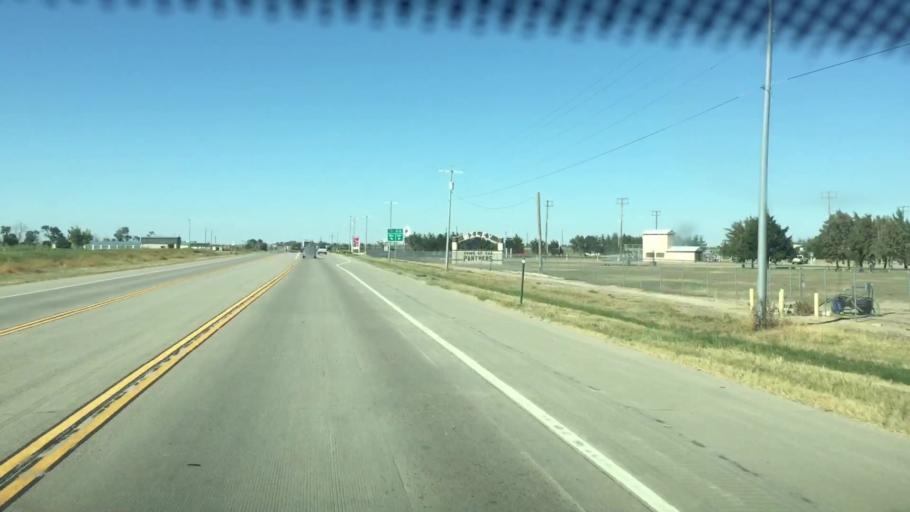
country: US
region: Colorado
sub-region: Prowers County
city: Lamar
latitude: 38.1550
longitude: -102.7237
